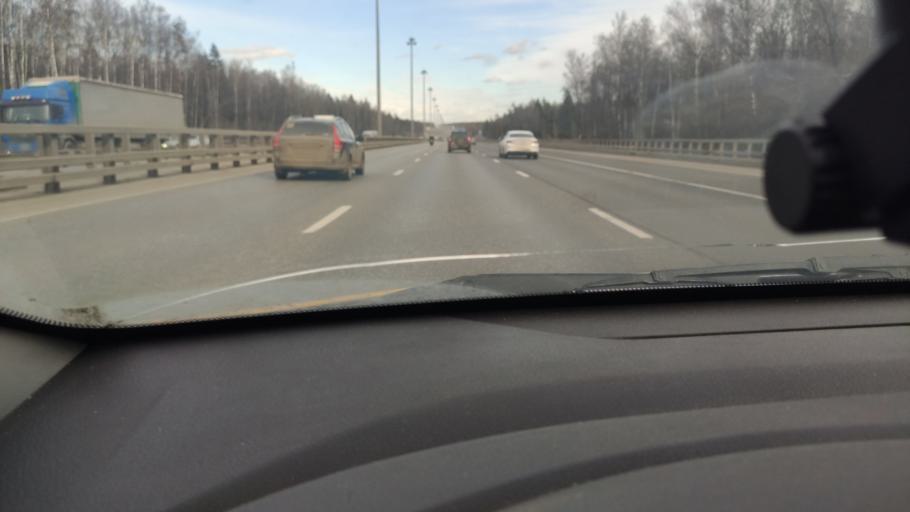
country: RU
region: Moscow
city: Vnukovo
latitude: 55.5750
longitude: 37.2212
